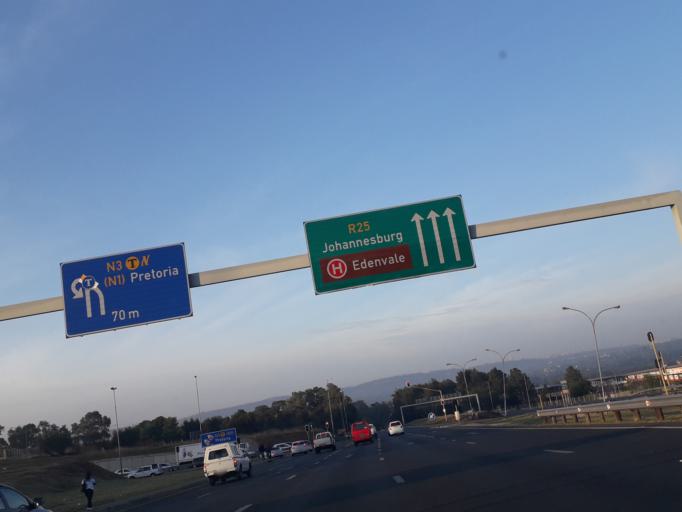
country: ZA
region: Gauteng
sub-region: City of Johannesburg Metropolitan Municipality
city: Modderfontein
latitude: -26.1228
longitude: 28.1354
